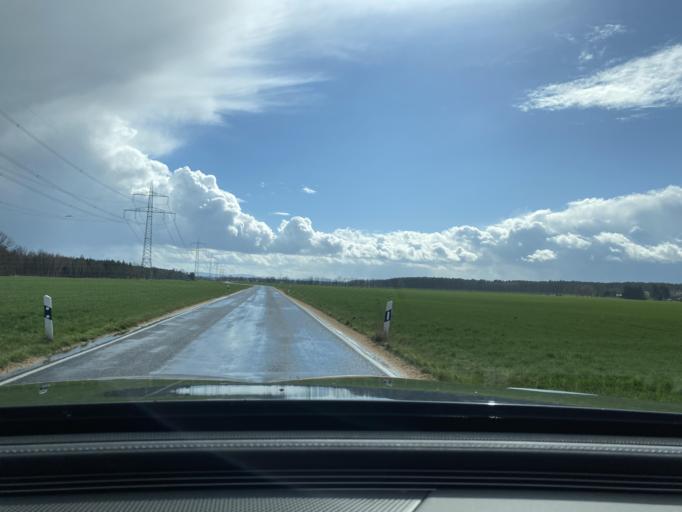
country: DE
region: Saxony
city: Grossdubrau
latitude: 51.2919
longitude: 14.4439
